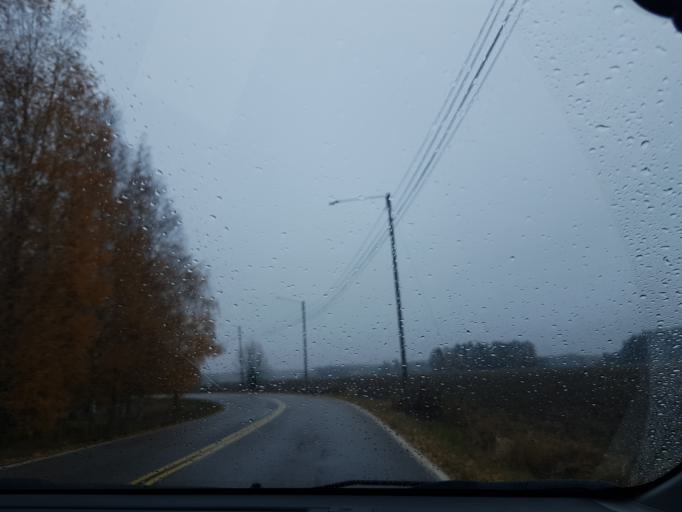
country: FI
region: Uusimaa
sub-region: Helsinki
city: Maentsaelae
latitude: 60.6149
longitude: 25.2327
